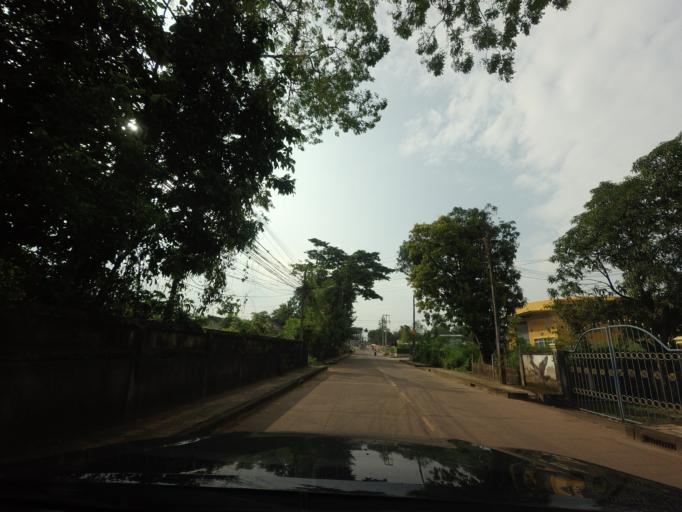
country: TH
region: Nong Khai
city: Nong Khai
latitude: 17.8795
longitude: 102.7462
